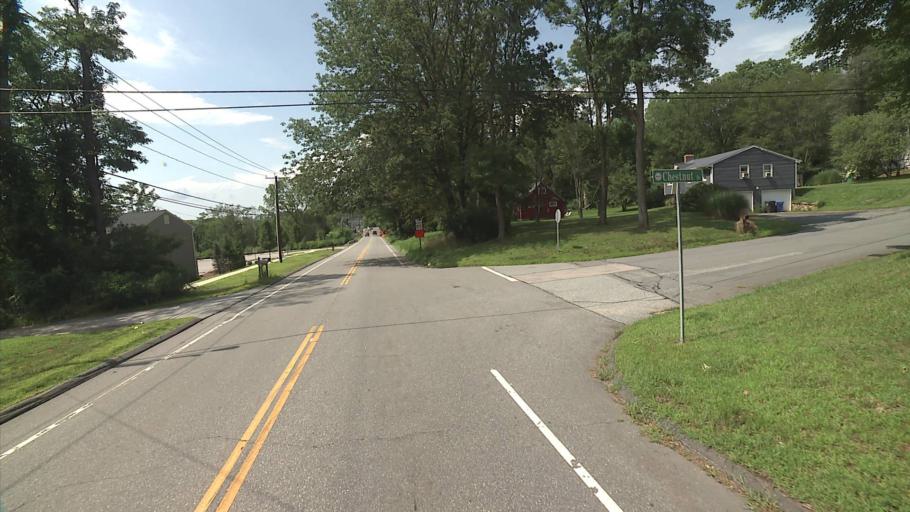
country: US
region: Connecticut
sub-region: New London County
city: Colchester
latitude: 41.5647
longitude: -72.3203
